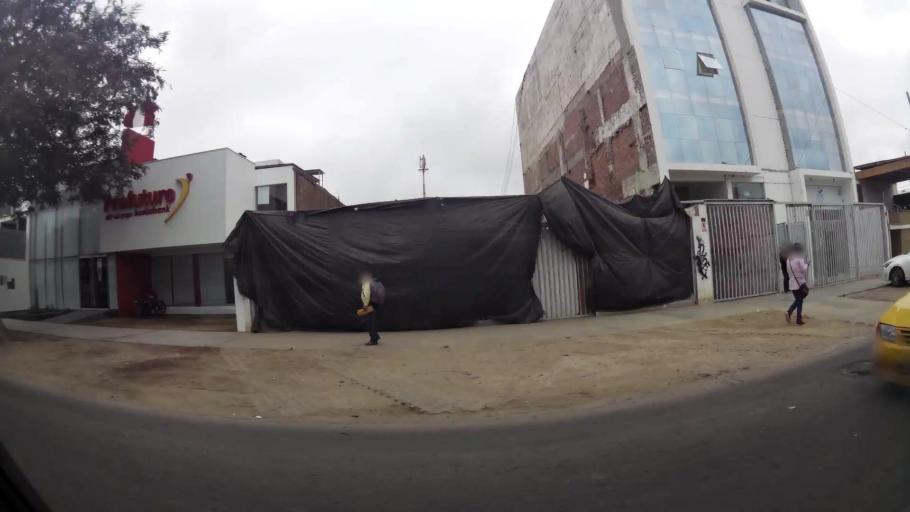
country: PE
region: La Libertad
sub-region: Provincia de Trujillo
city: Trujillo
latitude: -8.1193
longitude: -79.0342
